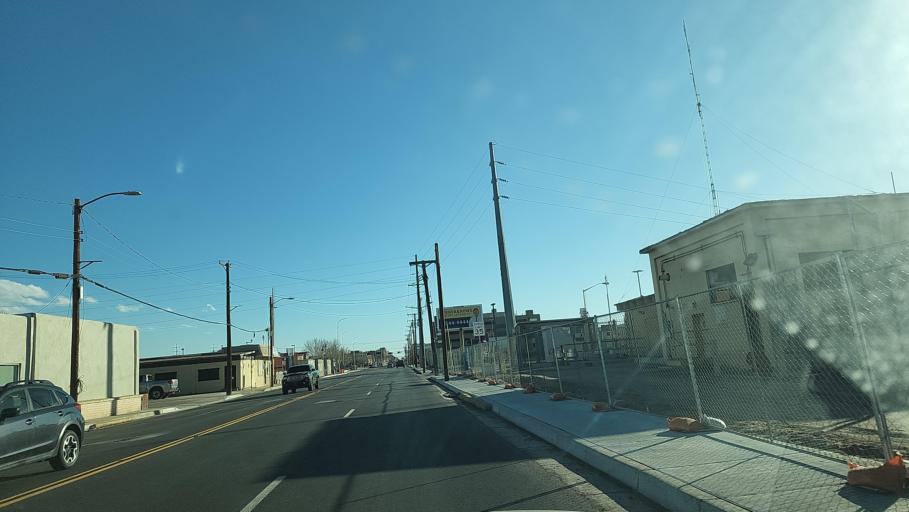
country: US
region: New Mexico
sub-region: Bernalillo County
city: Albuquerque
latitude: 35.0927
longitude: -106.6429
